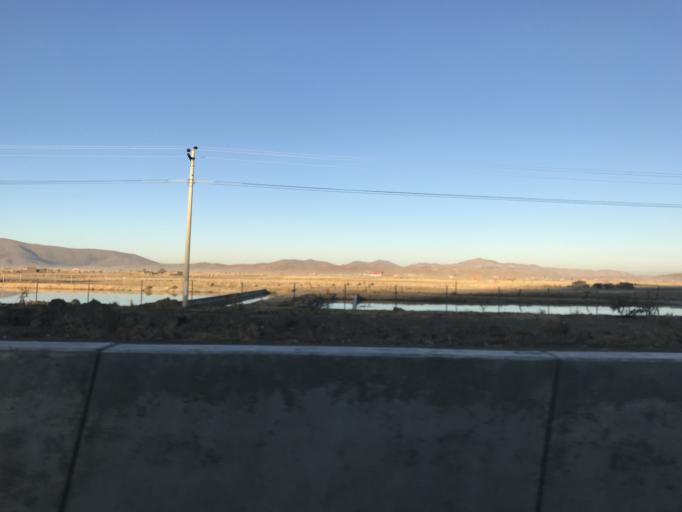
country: BO
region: La Paz
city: Batallas
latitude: -16.2919
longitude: -68.5403
